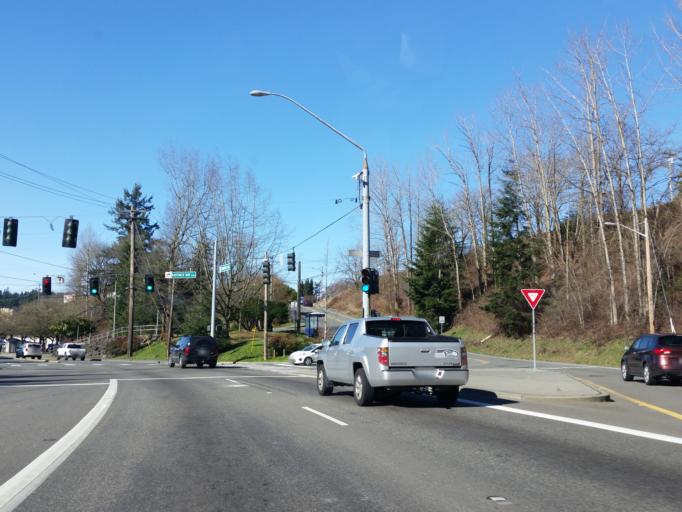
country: US
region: Washington
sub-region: King County
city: Bothell
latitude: 47.7591
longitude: -122.1991
